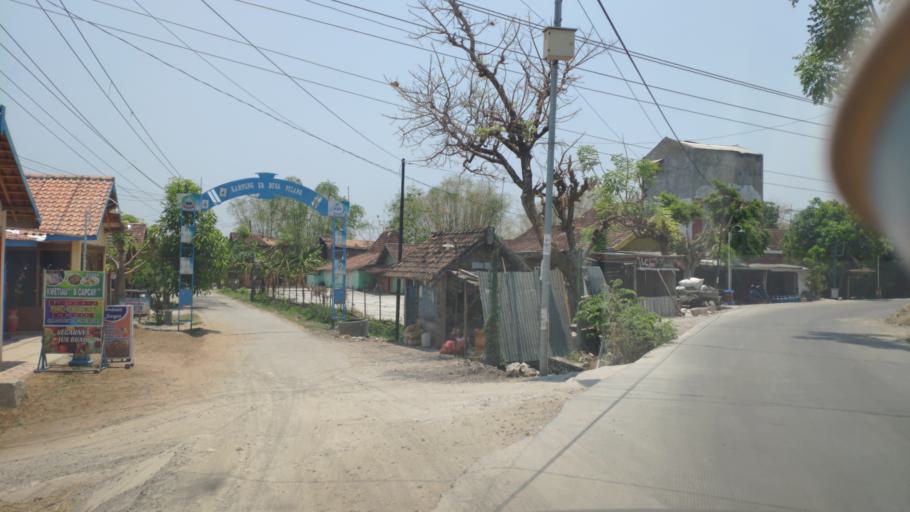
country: ID
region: Central Java
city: Pilang
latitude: -7.2046
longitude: 111.4013
